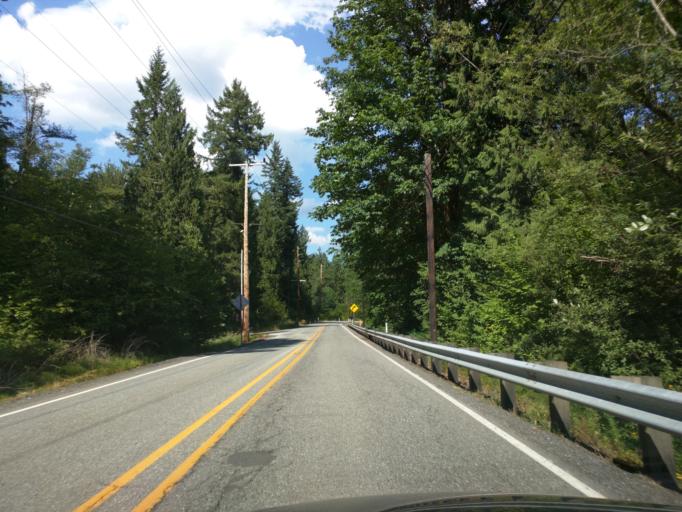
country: US
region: Washington
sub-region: Whatcom County
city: Peaceful Valley
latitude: 48.9186
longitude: -122.0999
